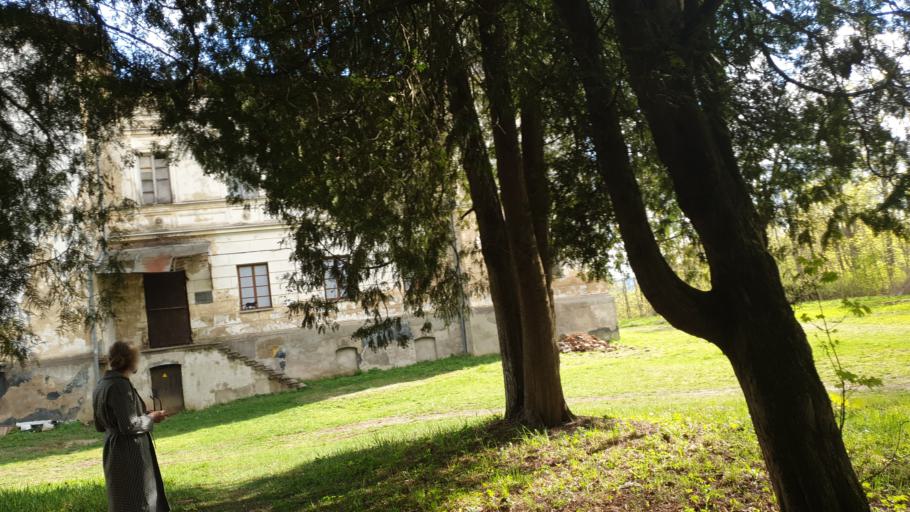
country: LT
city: Vilkija
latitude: 55.0801
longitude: 23.3905
